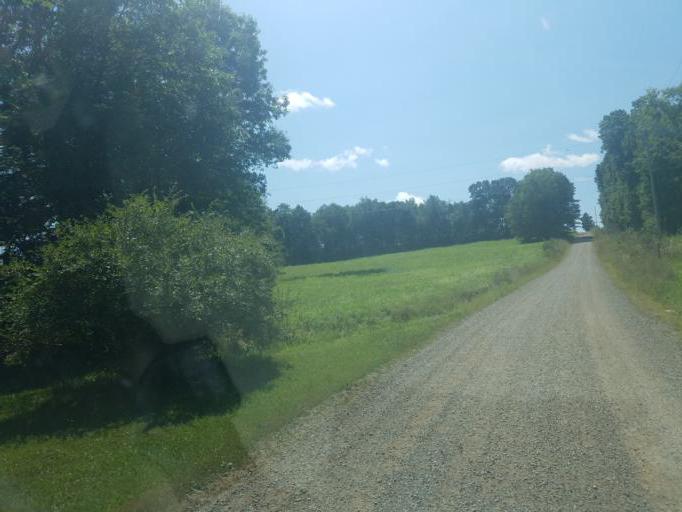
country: US
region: Pennsylvania
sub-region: Clarion County
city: Knox
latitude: 41.2066
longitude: -79.5767
